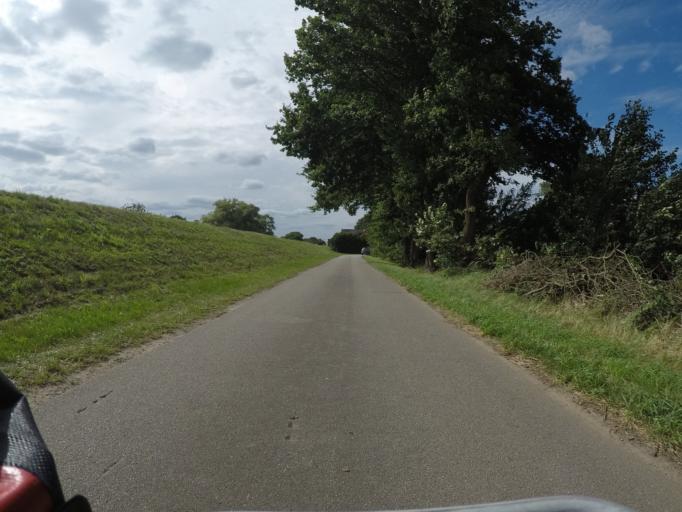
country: DE
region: Lower Saxony
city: Wittorf
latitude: 53.3508
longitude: 10.3764
